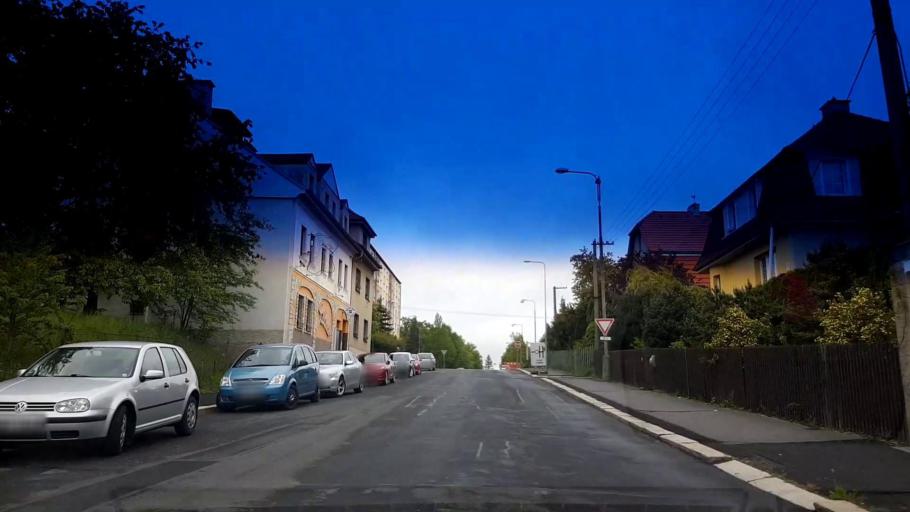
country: CZ
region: Karlovarsky
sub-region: Okres Cheb
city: Cheb
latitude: 50.0682
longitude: 12.3708
